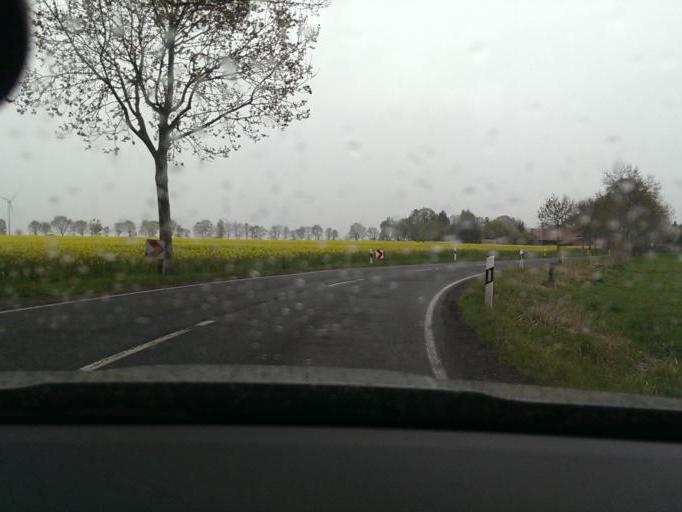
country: DE
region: Lower Saxony
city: Steimbke
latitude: 52.6201
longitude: 9.4879
